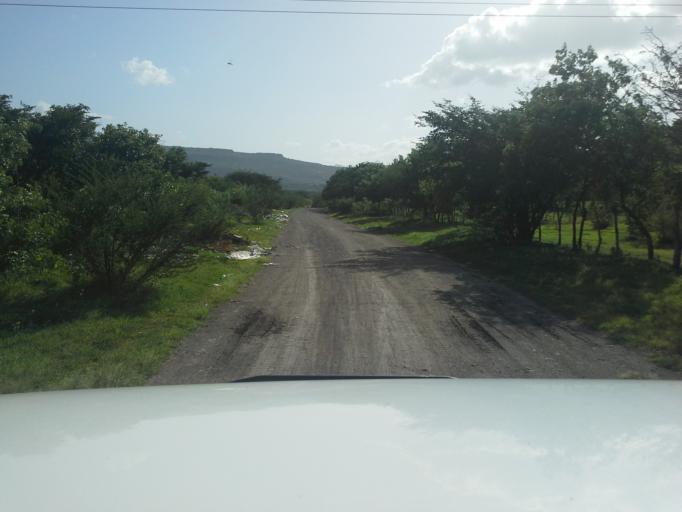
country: NI
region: Matagalpa
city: Ciudad Dario
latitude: 12.6590
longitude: -86.0759
